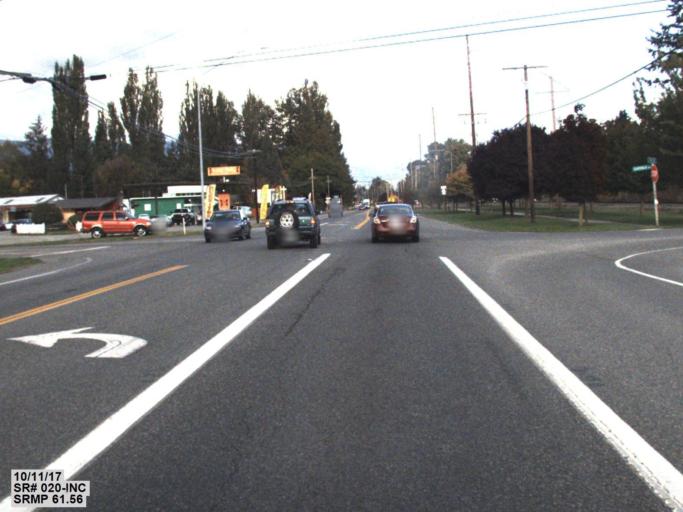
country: US
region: Washington
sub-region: Skagit County
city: Burlington
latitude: 48.4822
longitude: -122.3089
